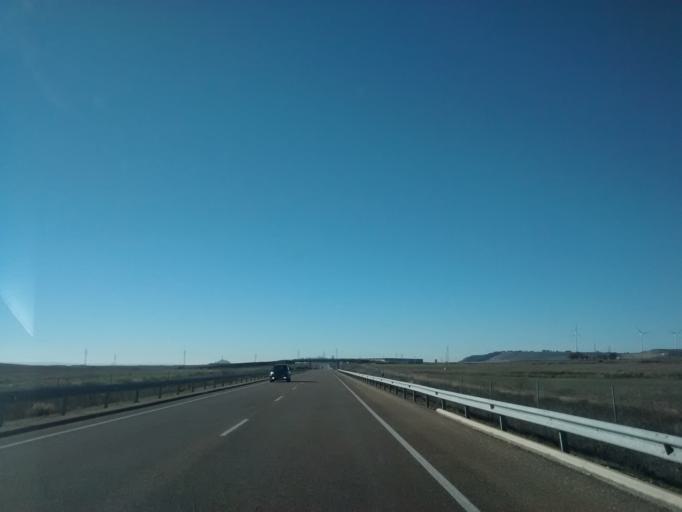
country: ES
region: Castille and Leon
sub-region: Provincia de Palencia
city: Fuentes de Valdepero
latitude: 42.0555
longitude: -4.5003
